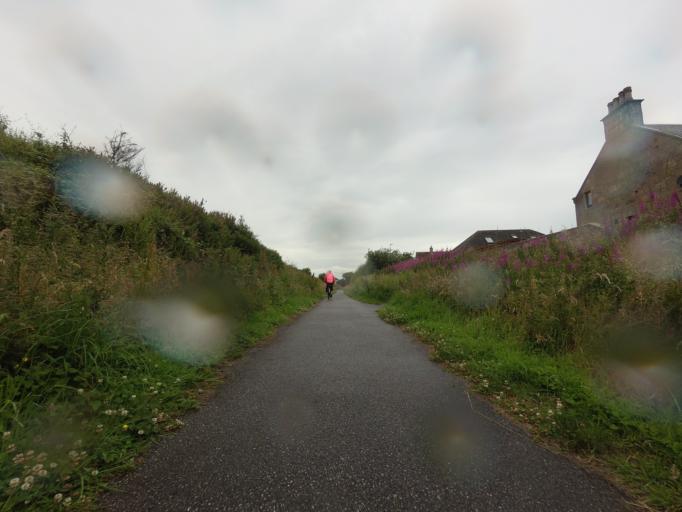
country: GB
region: Scotland
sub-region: Moray
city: Buckie
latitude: 57.6838
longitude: -2.9362
